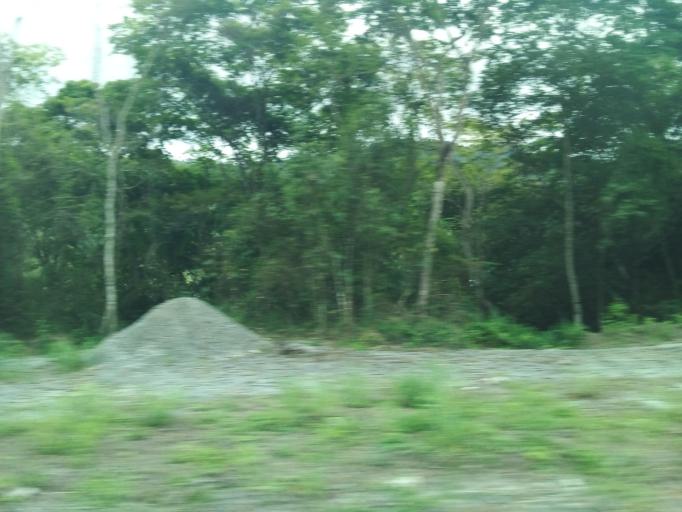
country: BR
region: Minas Gerais
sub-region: Nova Era
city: Nova Era
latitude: -19.6628
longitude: -42.8863
